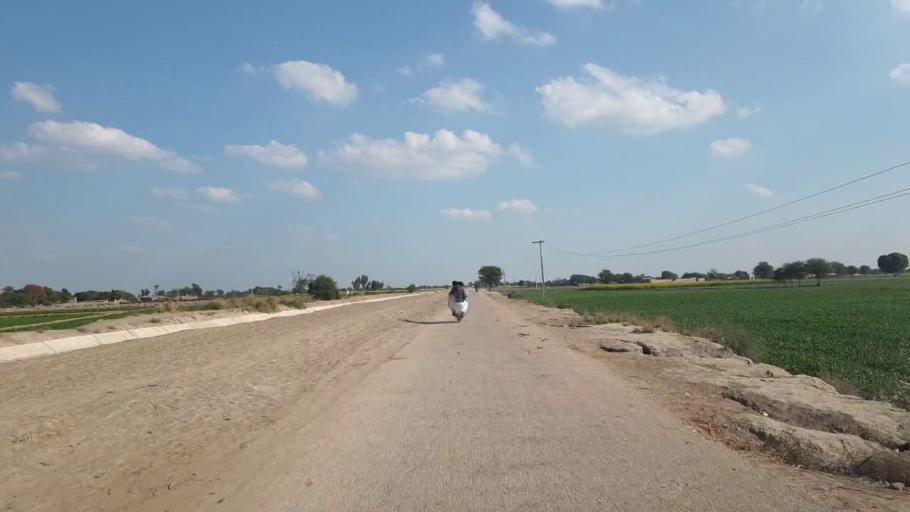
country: PK
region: Sindh
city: Shahpur Chakar
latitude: 26.1107
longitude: 68.5685
